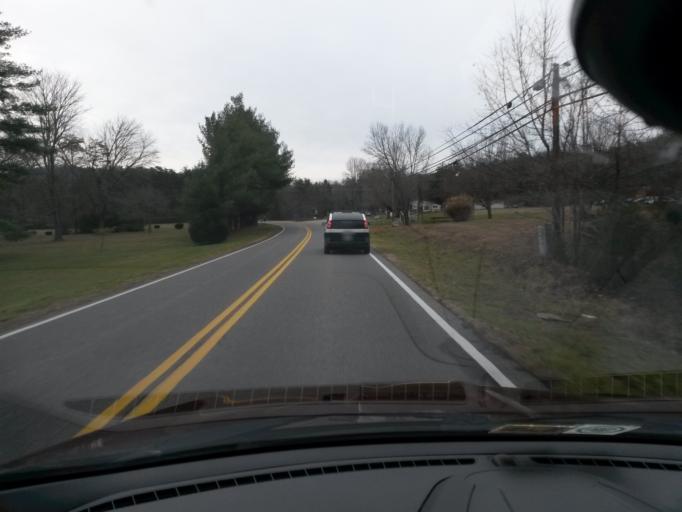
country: US
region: Virginia
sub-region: Alleghany County
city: Clifton Forge
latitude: 37.8115
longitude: -79.7431
